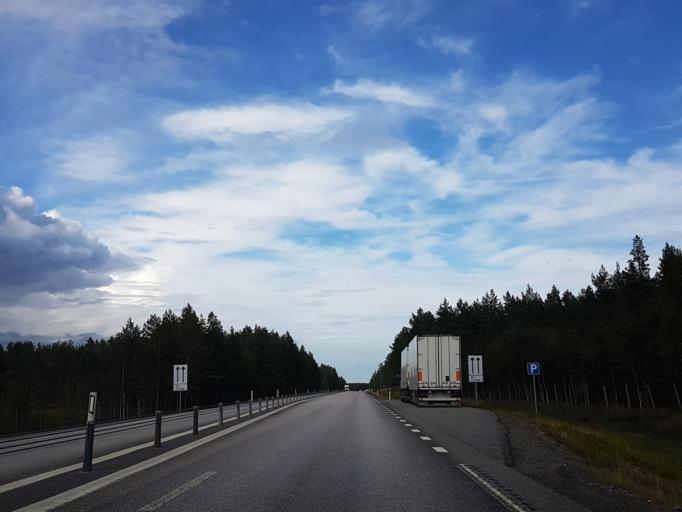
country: SE
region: Vaesterbotten
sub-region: Umea Kommun
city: Saevar
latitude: 63.9739
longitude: 20.7163
